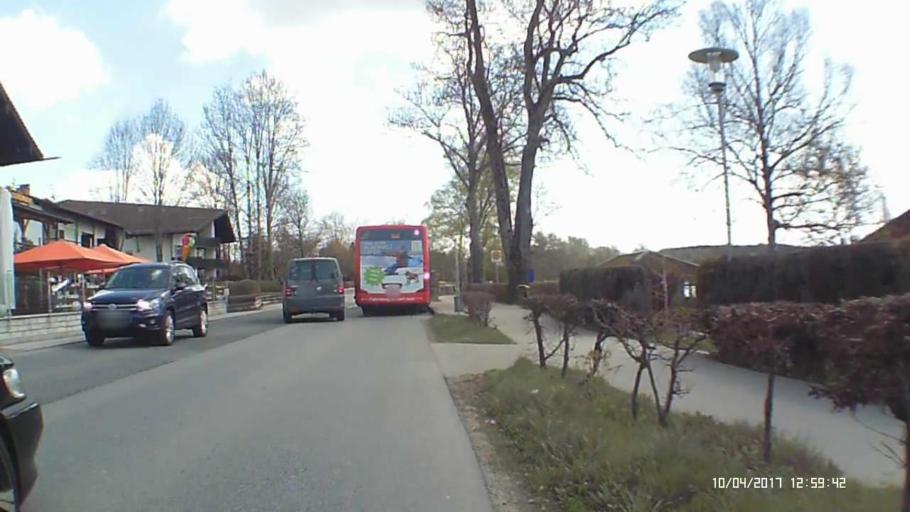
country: DE
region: Bavaria
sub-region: Upper Bavaria
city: Seeon-Seebruck
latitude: 47.9333
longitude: 12.4812
